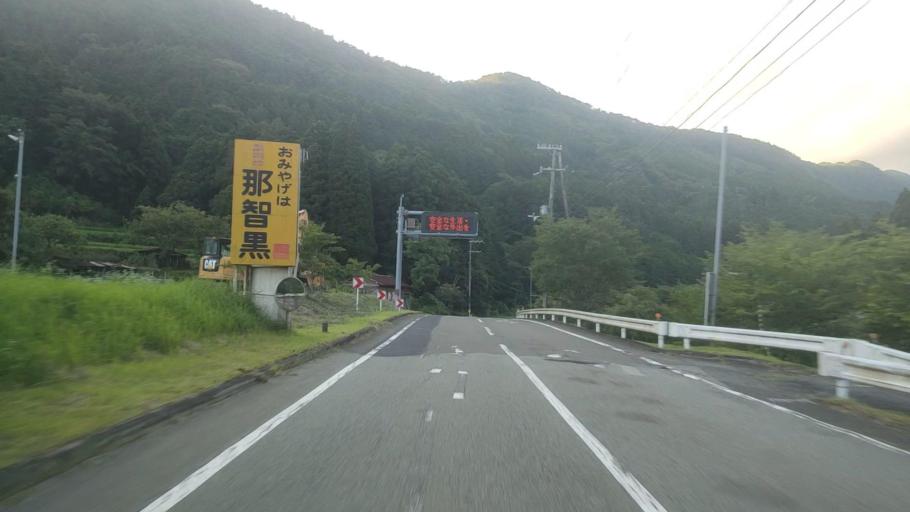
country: JP
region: Wakayama
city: Tanabe
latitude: 33.8237
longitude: 135.6314
